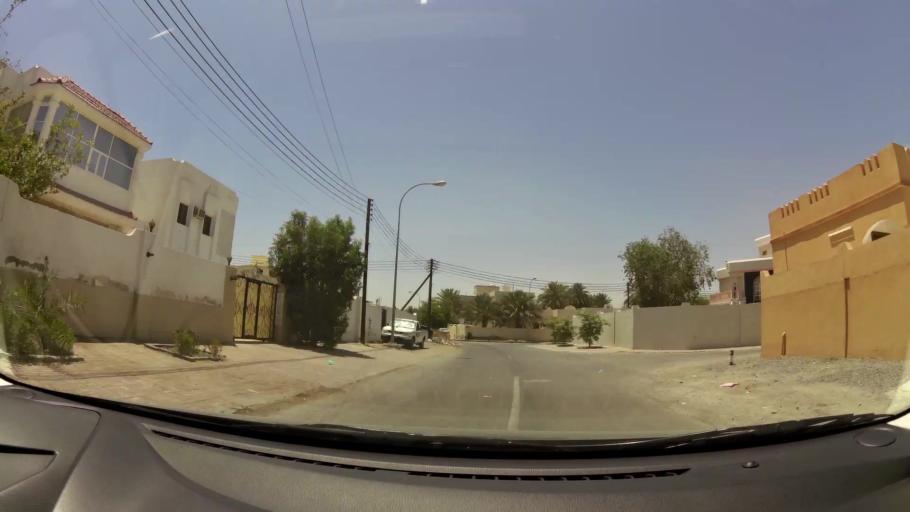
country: OM
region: Muhafazat Masqat
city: As Sib al Jadidah
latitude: 23.6266
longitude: 58.2419
